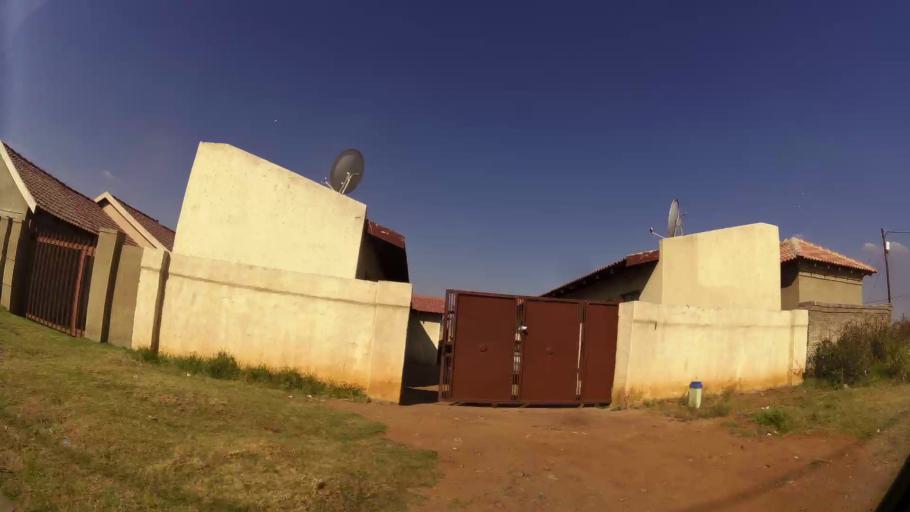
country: ZA
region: Gauteng
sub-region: Ekurhuleni Metropolitan Municipality
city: Benoni
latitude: -26.2287
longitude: 28.3262
